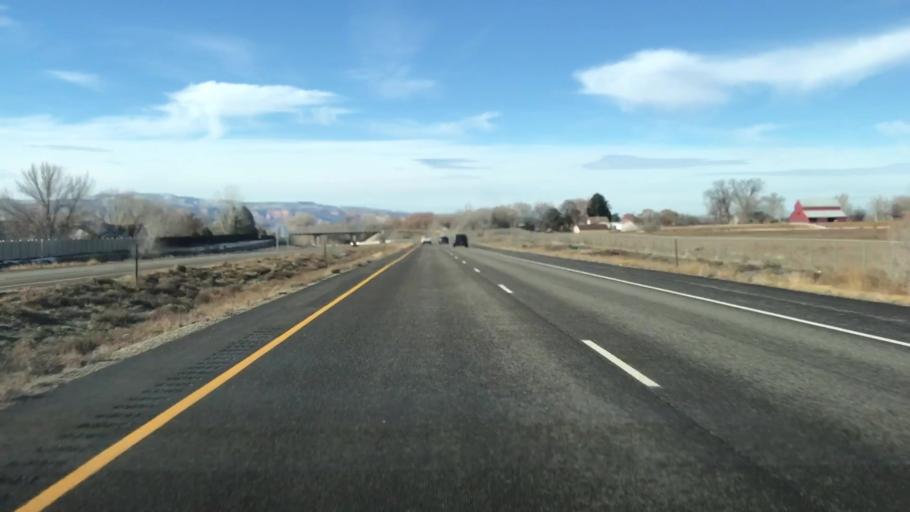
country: US
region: Colorado
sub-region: Mesa County
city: Grand Junction
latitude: 39.1159
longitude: -108.5568
